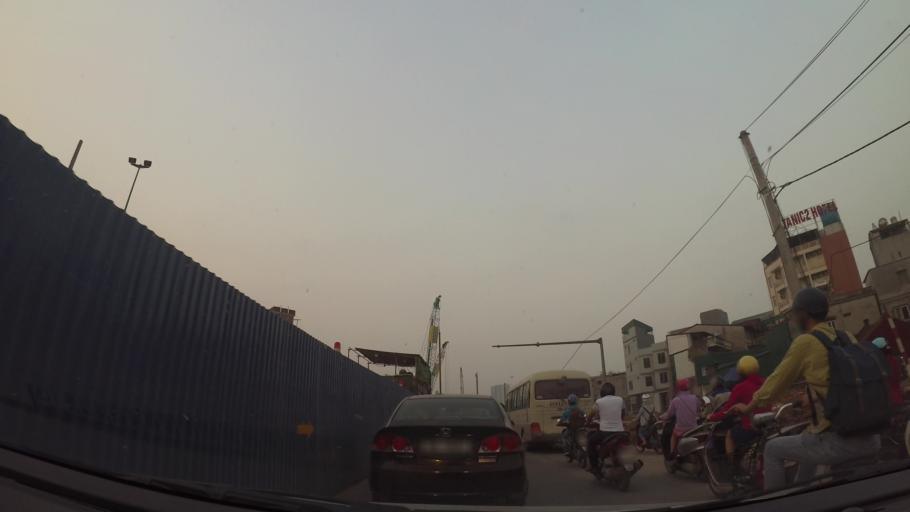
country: VN
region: Ha Noi
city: Cau Dien
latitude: 21.0591
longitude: 105.7831
